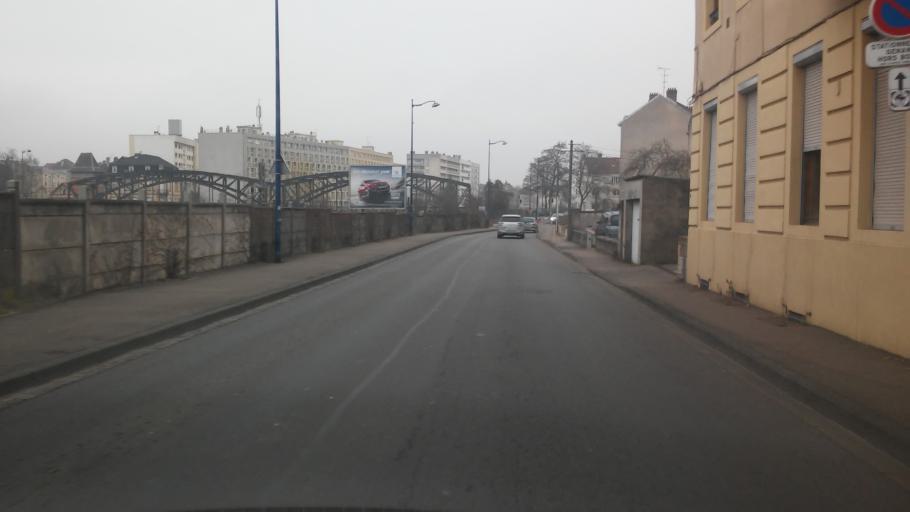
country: FR
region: Lorraine
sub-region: Departement de la Moselle
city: Montigny-les-Metz
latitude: 49.1003
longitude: 6.1688
